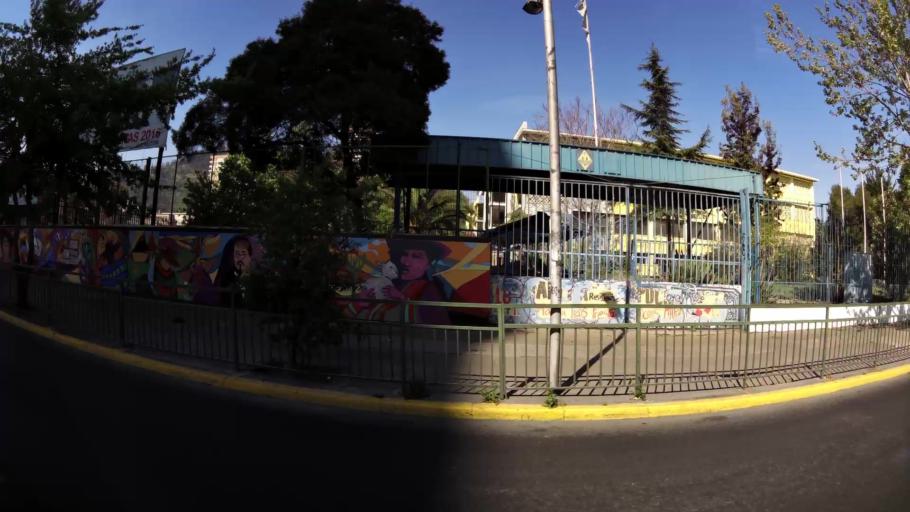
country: CL
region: Santiago Metropolitan
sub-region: Provincia de Santiago
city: Santiago
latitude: -33.4263
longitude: -70.6460
